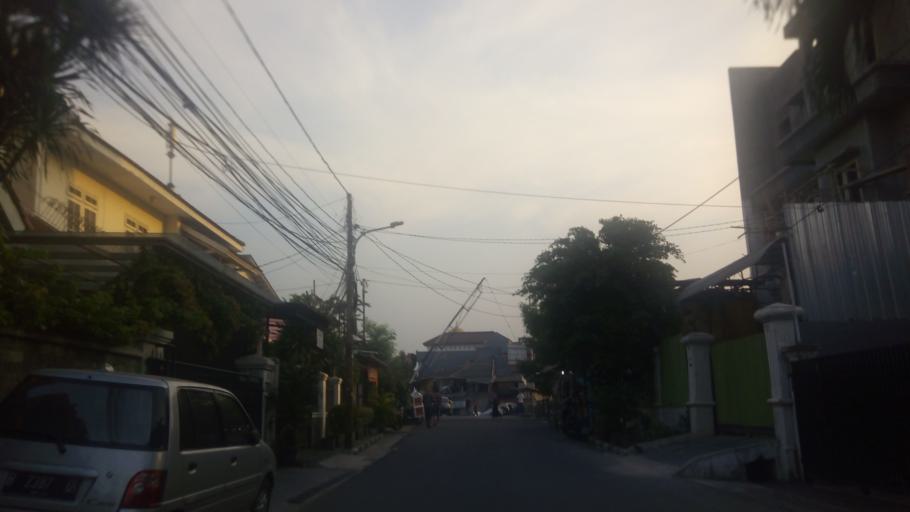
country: ID
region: Jakarta Raya
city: Jakarta
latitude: -6.1993
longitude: 106.8504
